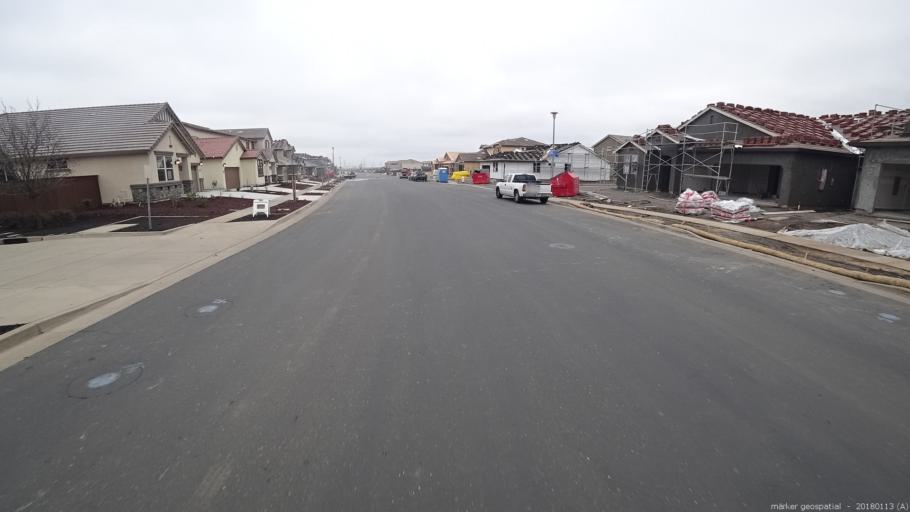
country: US
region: California
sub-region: Sacramento County
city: Gold River
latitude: 38.5665
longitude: -121.1993
